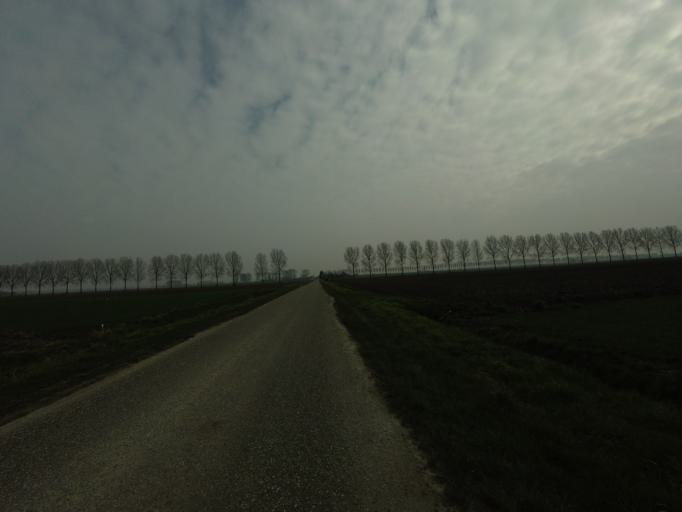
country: BE
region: Flanders
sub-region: Provincie Oost-Vlaanderen
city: Sint-Gillis-Waas
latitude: 51.3211
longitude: 4.1909
